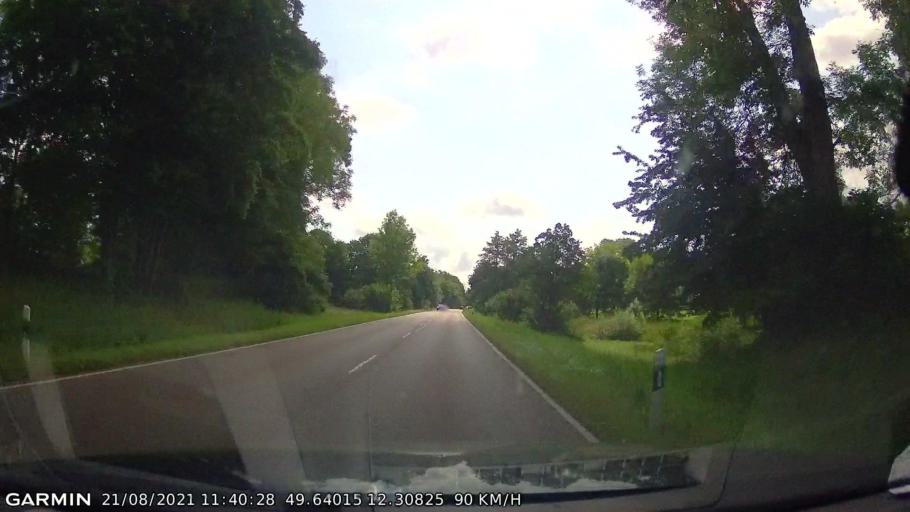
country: DE
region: Bavaria
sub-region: Upper Palatinate
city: Vohenstrauss
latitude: 49.6401
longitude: 12.3084
